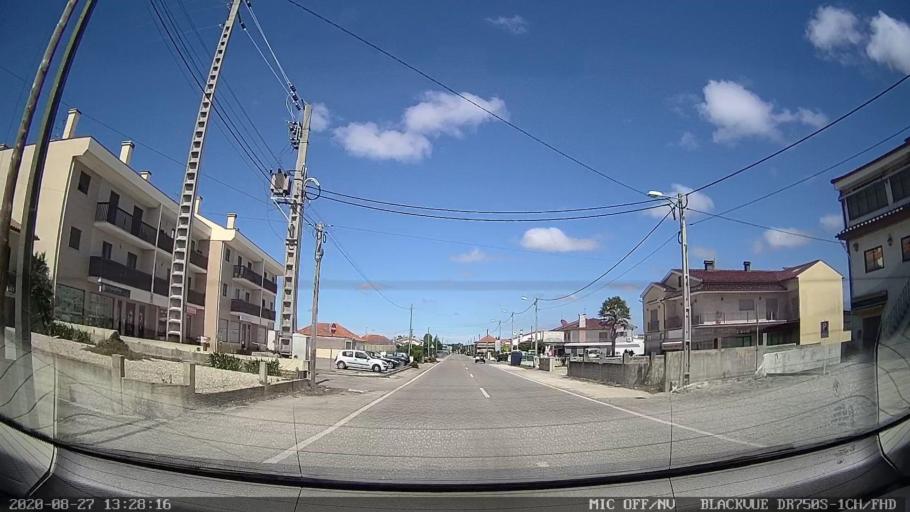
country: PT
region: Aveiro
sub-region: Vagos
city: Vagos
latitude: 40.5223
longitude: -8.6794
